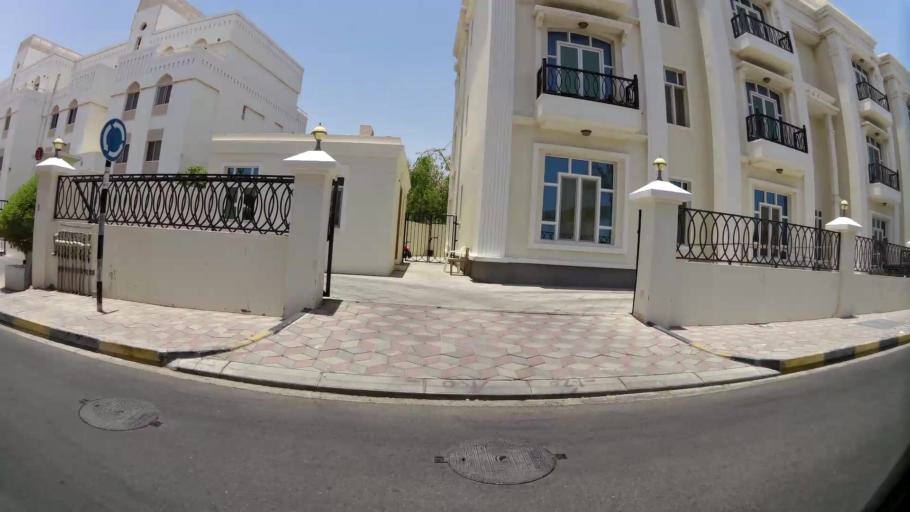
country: OM
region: Muhafazat Masqat
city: Bawshar
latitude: 23.5992
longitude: 58.4548
